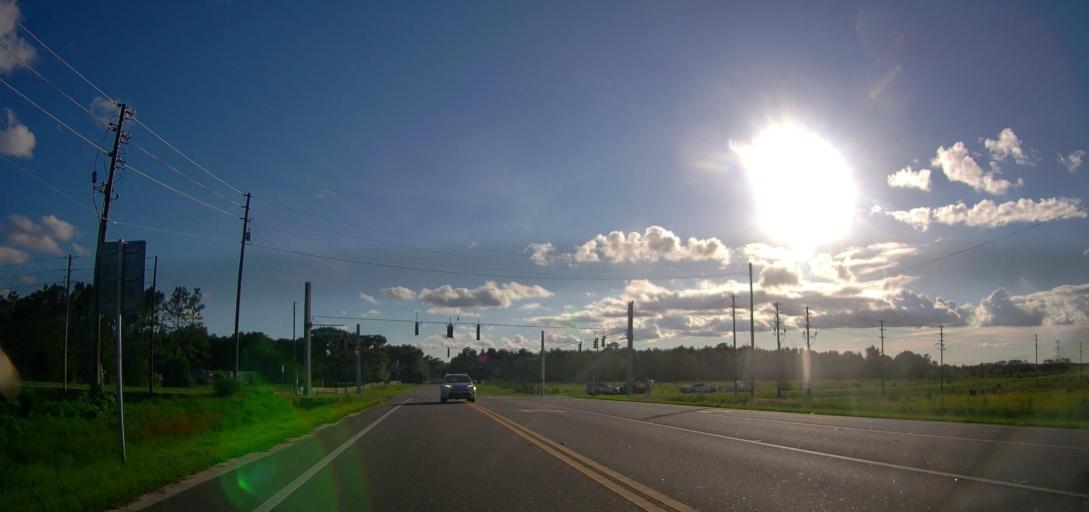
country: US
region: Florida
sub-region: Marion County
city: Silver Springs Shores
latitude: 29.0639
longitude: -82.0169
